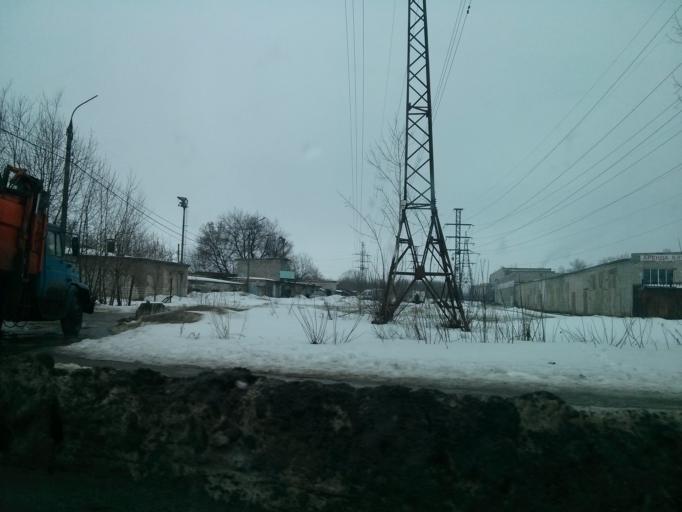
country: RU
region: Vladimir
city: Murom
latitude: 55.5581
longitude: 42.0596
